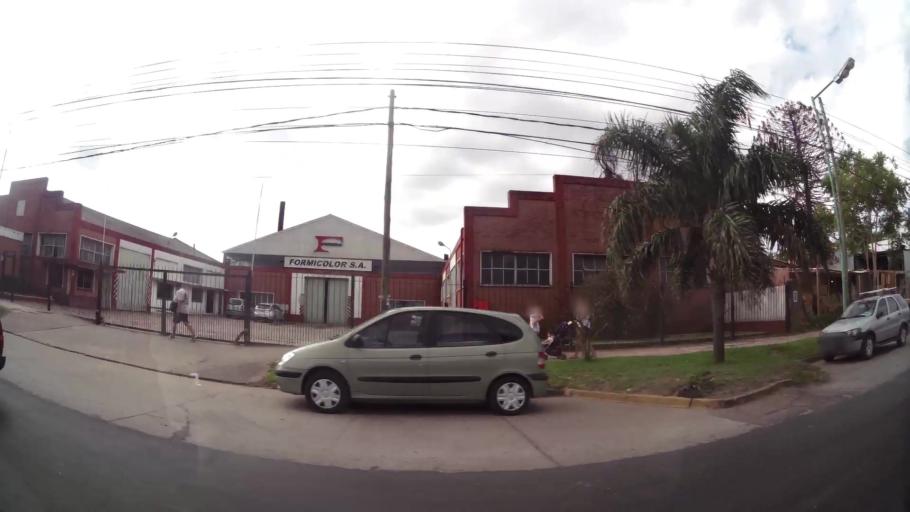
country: AR
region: Buenos Aires
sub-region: Partido de Tigre
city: Tigre
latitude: -34.4734
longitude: -58.6587
